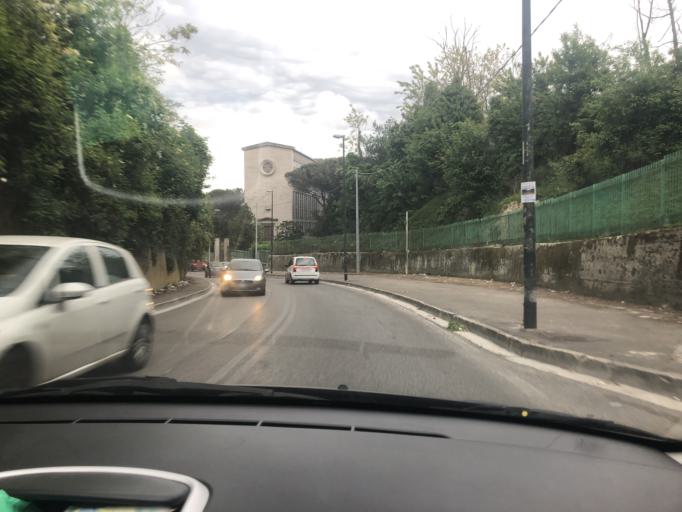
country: IT
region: Campania
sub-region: Provincia di Napoli
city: Napoli
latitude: 40.8628
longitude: 14.2129
